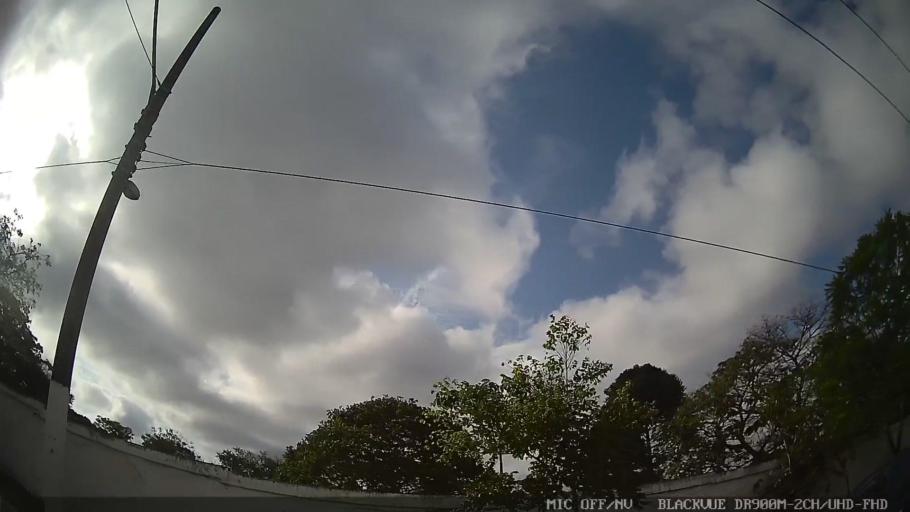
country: BR
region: Sao Paulo
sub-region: Sao Caetano Do Sul
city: Sao Caetano do Sul
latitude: -23.5656
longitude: -46.5254
